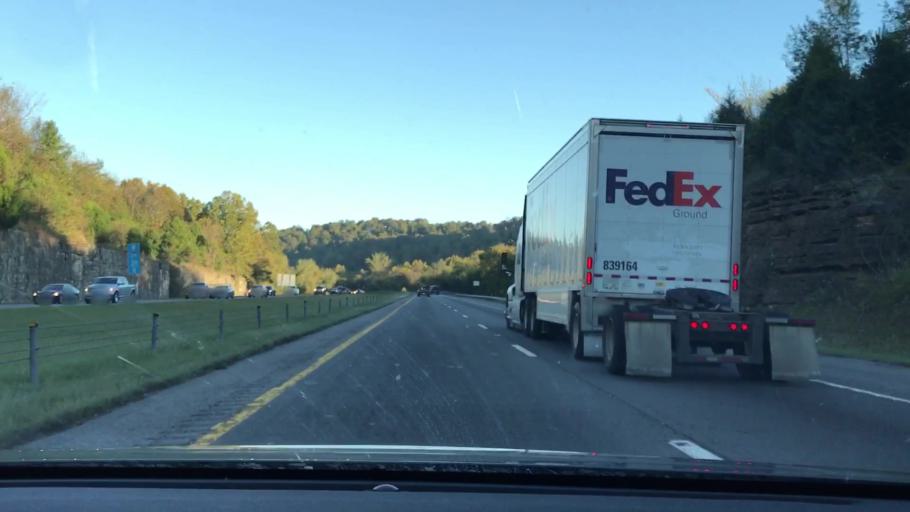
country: US
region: Tennessee
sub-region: Davidson County
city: Goodlettsville
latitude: 36.2988
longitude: -86.8116
